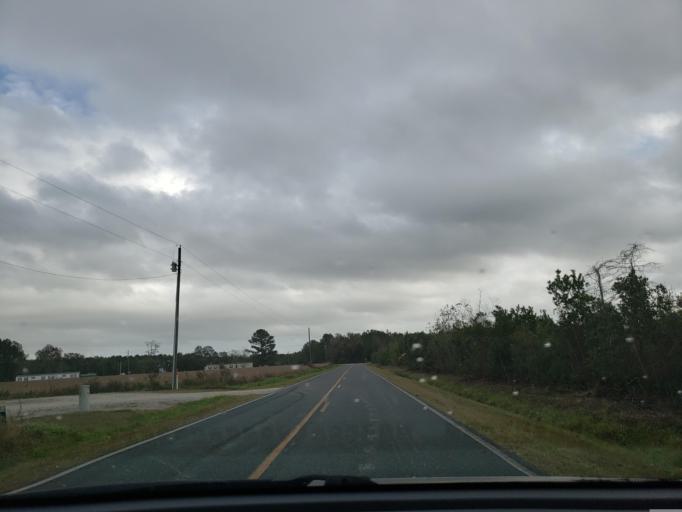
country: US
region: North Carolina
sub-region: Onslow County
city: Richlands
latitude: 34.7367
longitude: -77.6242
